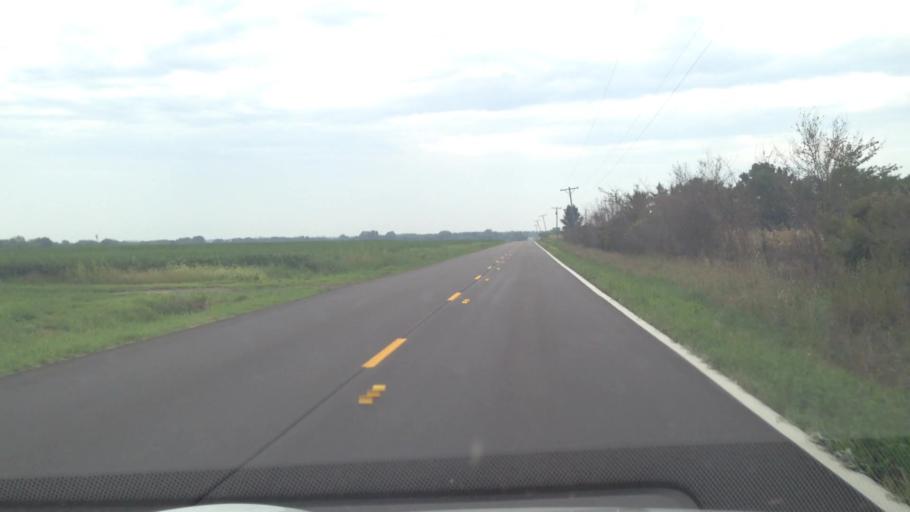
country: US
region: Kansas
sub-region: Crawford County
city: Girard
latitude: 37.6240
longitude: -94.9698
